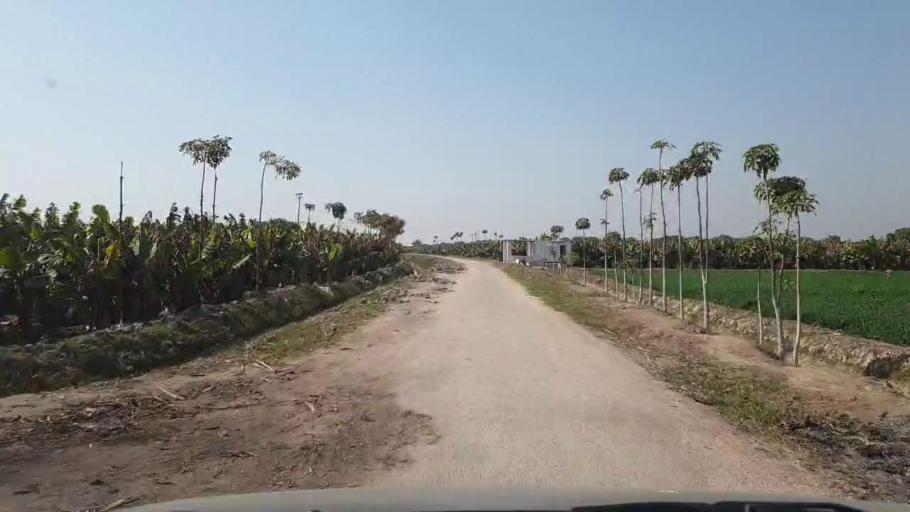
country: PK
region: Sindh
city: Tando Jam
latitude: 25.4128
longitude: 68.6275
